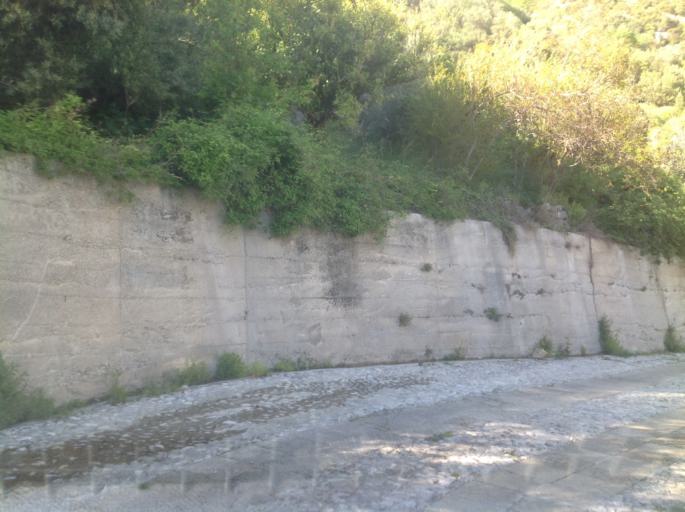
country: IT
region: Calabria
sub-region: Provincia di Cosenza
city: Civita
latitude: 39.8295
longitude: 16.3150
